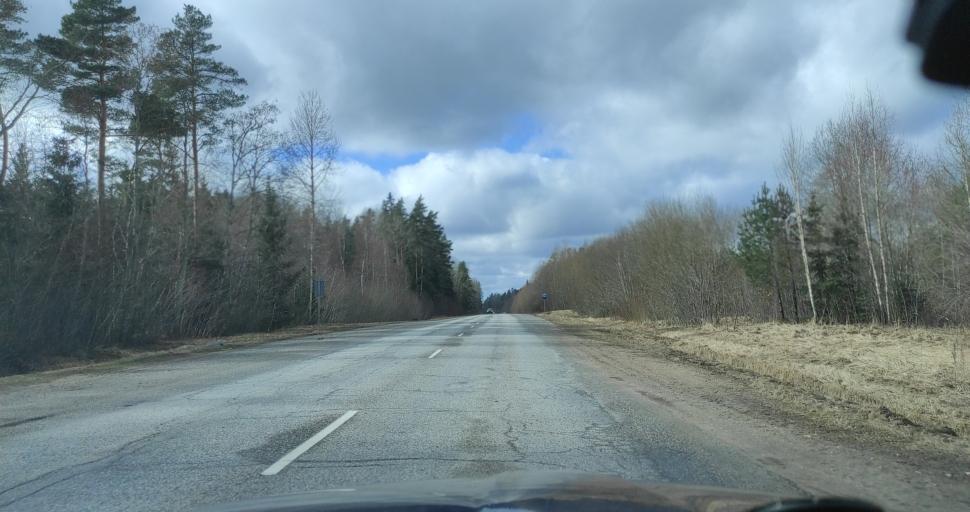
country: LV
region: Kuldigas Rajons
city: Kuldiga
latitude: 56.9826
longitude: 22.0435
